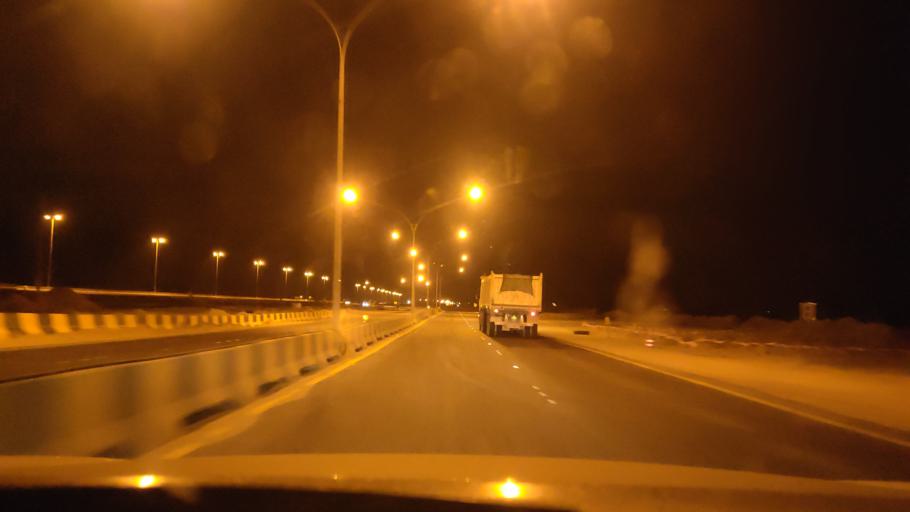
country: KW
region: Al Ahmadi
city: Al Ahmadi
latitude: 28.9121
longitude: 48.0961
